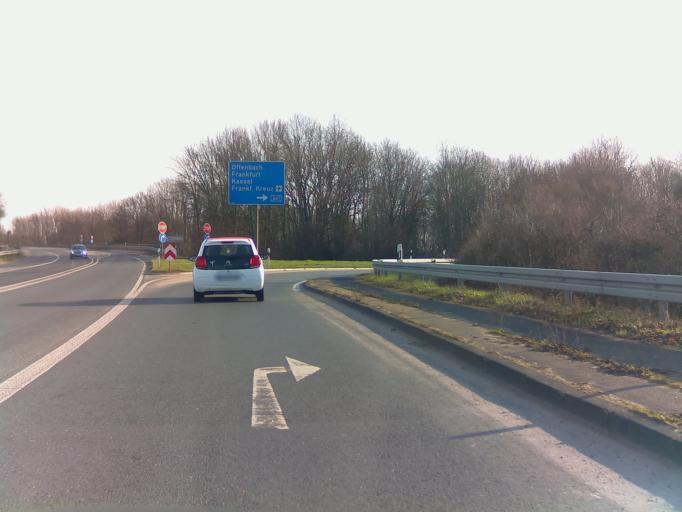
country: DE
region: Hesse
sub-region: Regierungsbezirk Darmstadt
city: Oberursel
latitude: 50.2140
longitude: 8.5746
